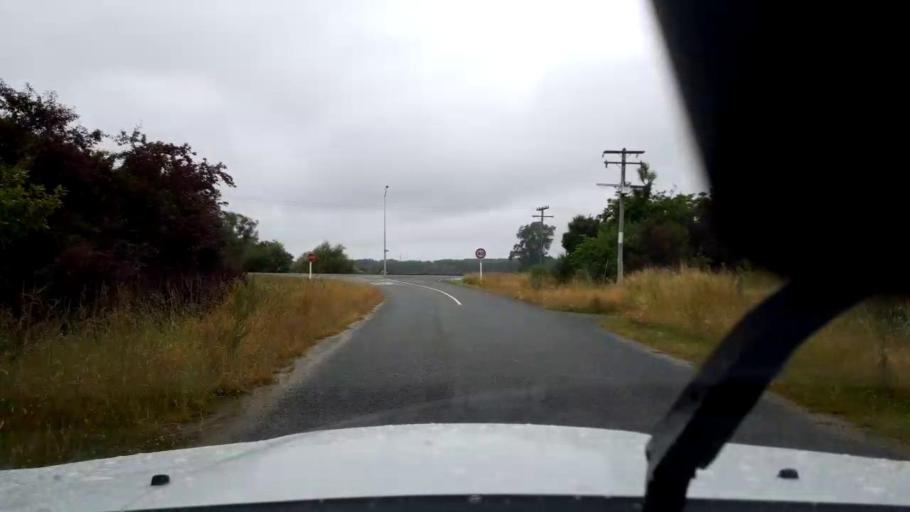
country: NZ
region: Canterbury
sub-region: Timaru District
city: Pleasant Point
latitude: -44.2547
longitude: 171.2744
